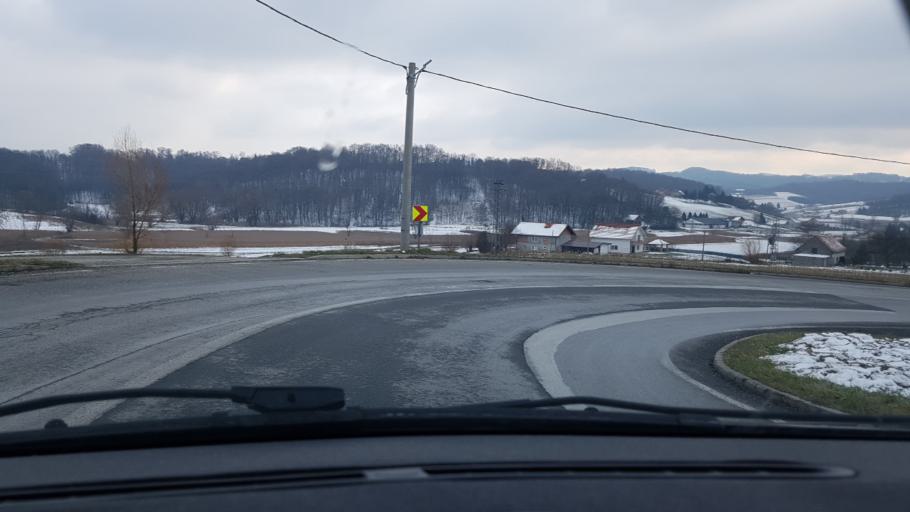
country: HR
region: Krapinsko-Zagorska
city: Mihovljan
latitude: 46.1522
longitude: 15.9635
